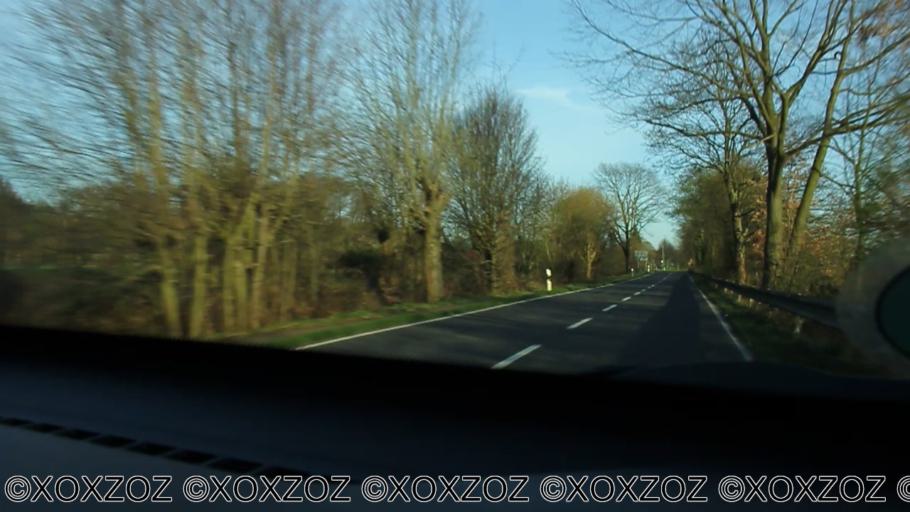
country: DE
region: North Rhine-Westphalia
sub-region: Regierungsbezirk Koln
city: Niederzier
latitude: 50.9070
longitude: 6.4388
